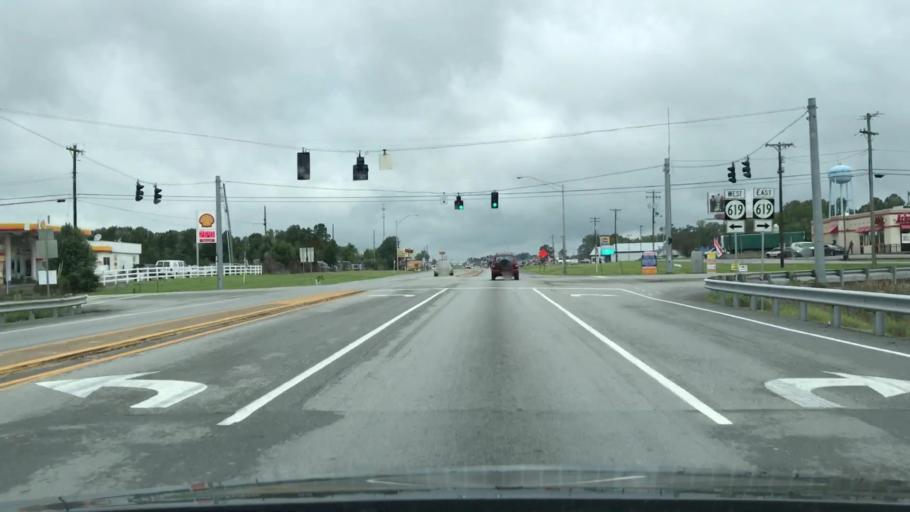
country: US
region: Kentucky
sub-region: Russell County
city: Russell Springs
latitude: 37.0549
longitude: -85.0702
